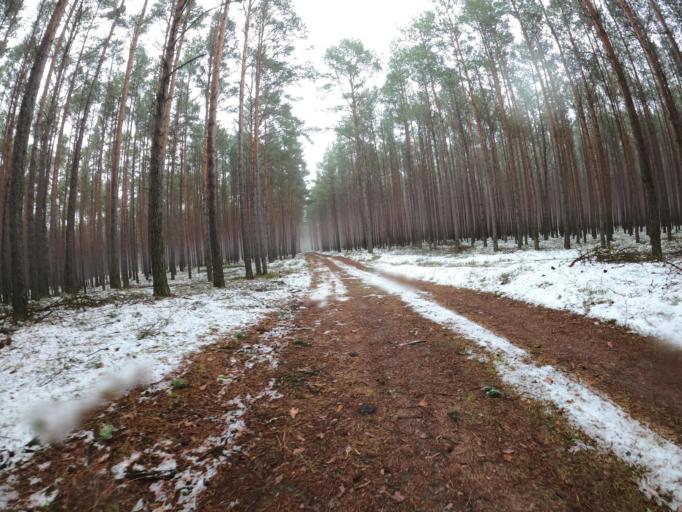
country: PL
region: Lubusz
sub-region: Powiat sulecinski
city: Torzym
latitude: 52.2134
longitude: 14.9719
